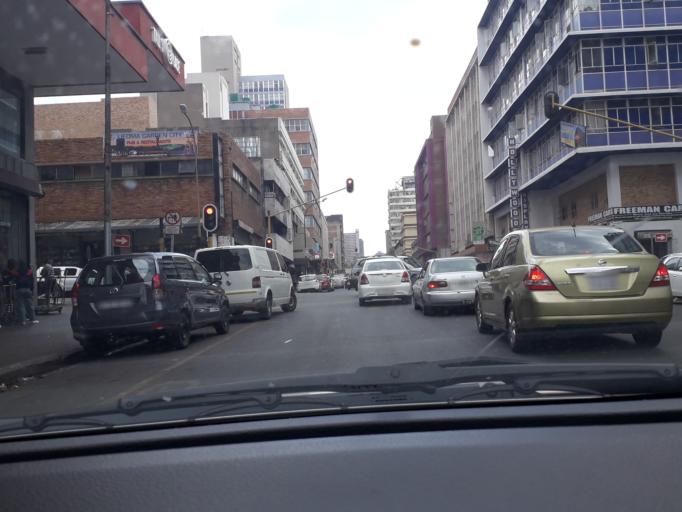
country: ZA
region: Gauteng
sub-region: City of Johannesburg Metropolitan Municipality
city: Johannesburg
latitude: -26.2031
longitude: 28.0526
